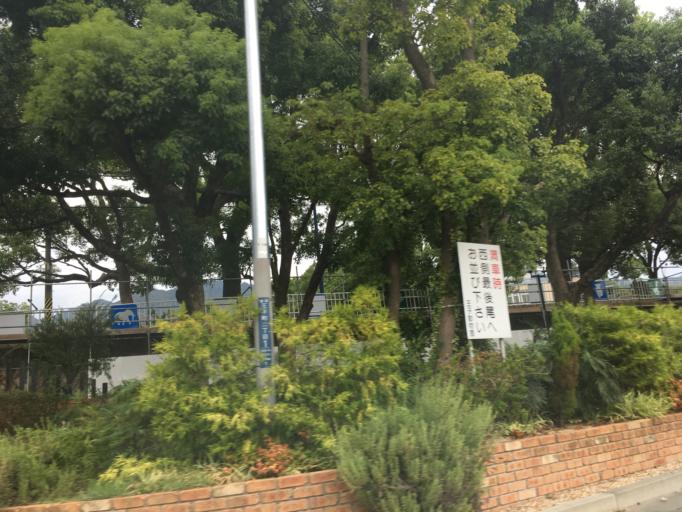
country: JP
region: Hyogo
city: Kobe
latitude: 34.7093
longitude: 135.2171
